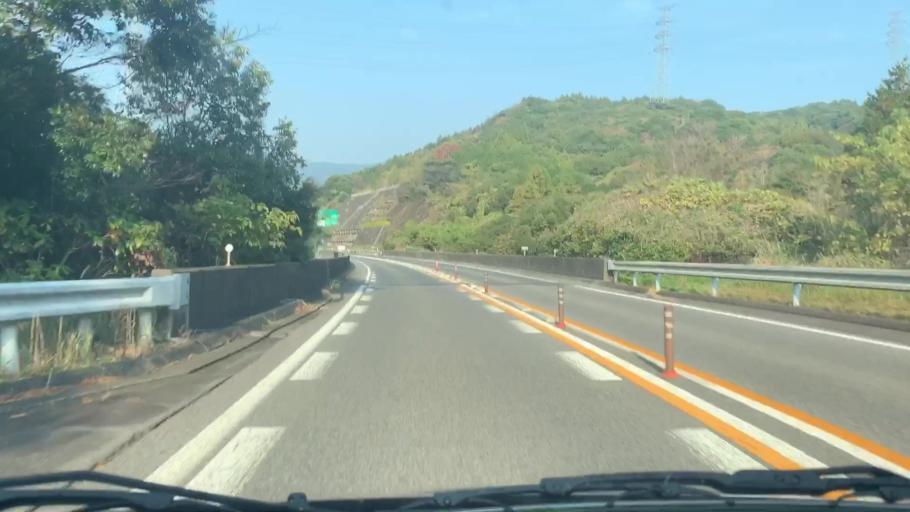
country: JP
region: Saga Prefecture
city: Imaricho-ko
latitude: 33.1649
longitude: 129.8616
